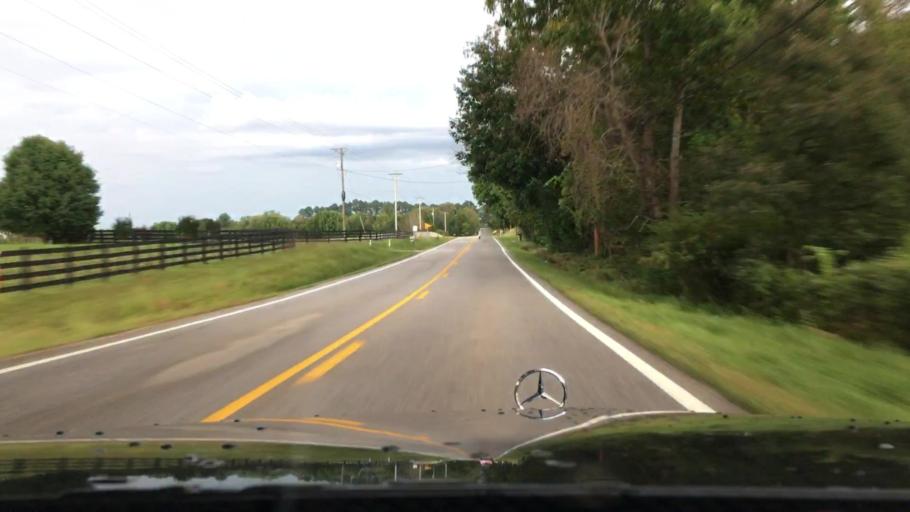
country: US
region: Virginia
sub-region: Amherst County
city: Amherst
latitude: 37.6274
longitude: -79.0175
